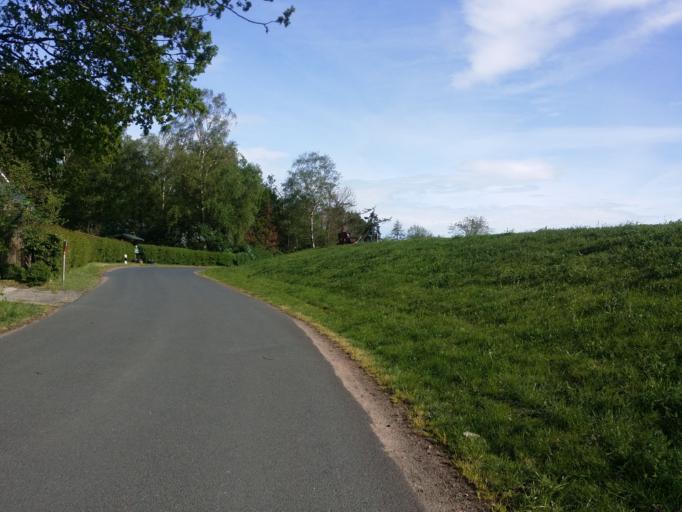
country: DE
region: Lower Saxony
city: Lemwerder
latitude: 53.1335
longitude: 8.6413
